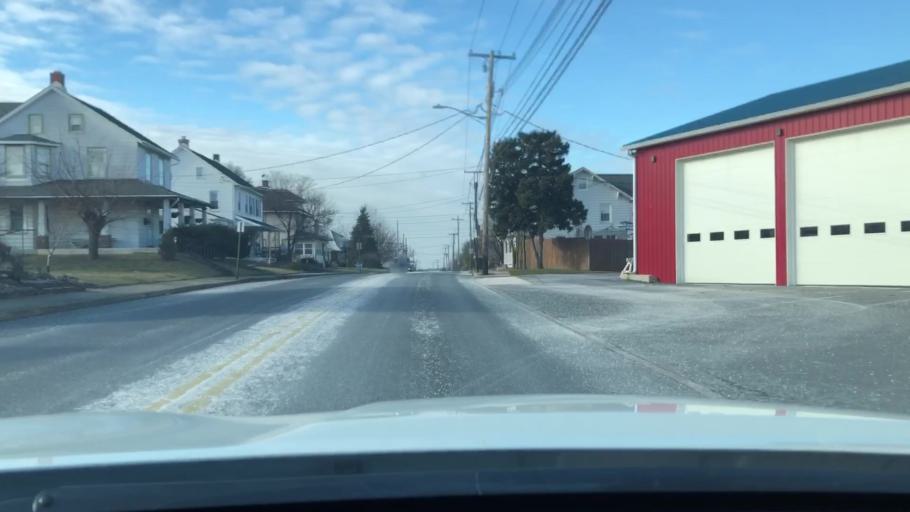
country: US
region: Pennsylvania
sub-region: Lehigh County
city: Catasauqua
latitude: 40.6462
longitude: -75.4769
